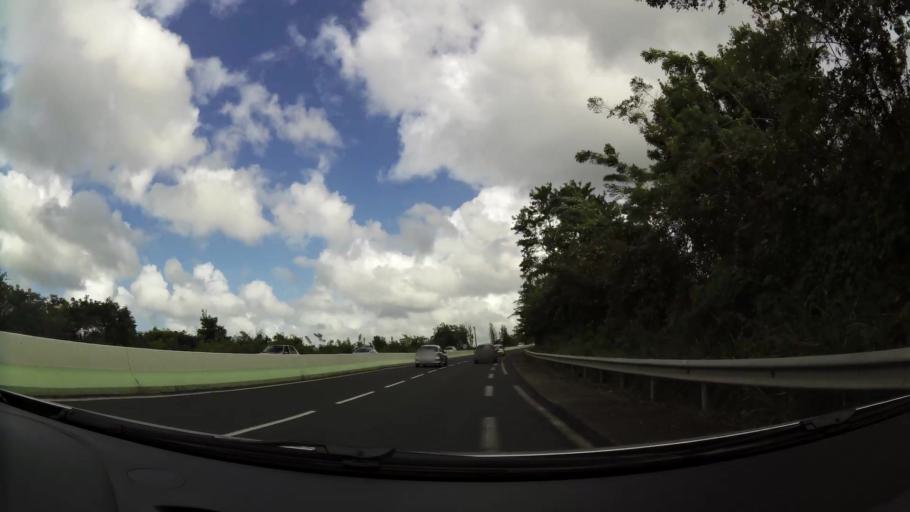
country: MQ
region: Martinique
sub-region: Martinique
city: Les Trois-Ilets
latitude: 14.5054
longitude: -60.9817
